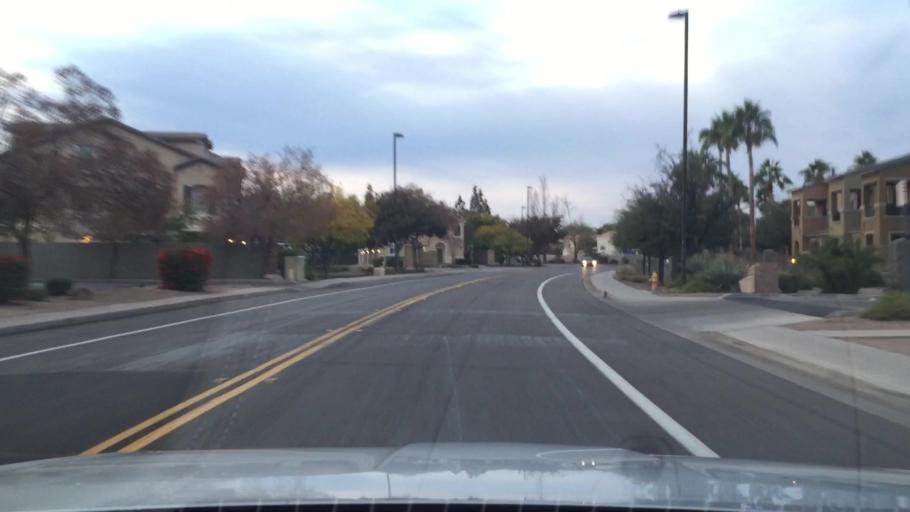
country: US
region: Arizona
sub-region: Maricopa County
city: Gilbert
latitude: 33.3597
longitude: -111.7920
